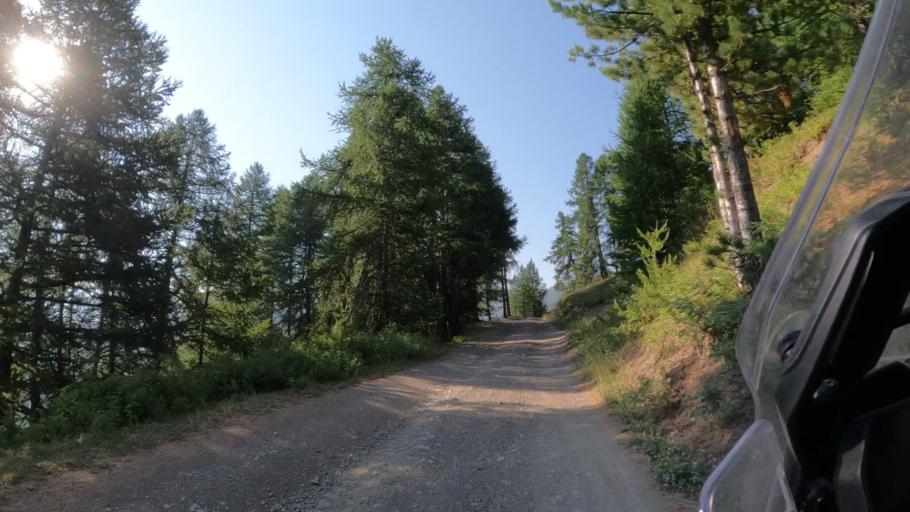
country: FR
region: Provence-Alpes-Cote d'Azur
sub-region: Departement des Hautes-Alpes
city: Guillestre
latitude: 44.6192
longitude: 6.6239
